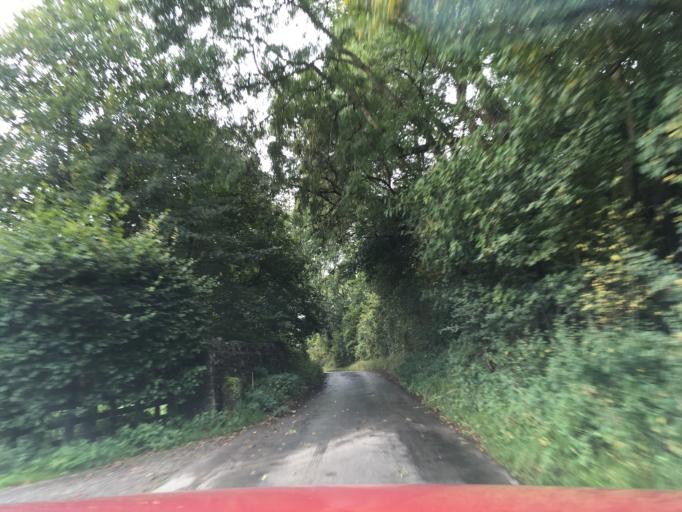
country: GB
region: England
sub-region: South Gloucestershire
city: Tytherington
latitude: 51.5957
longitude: -2.4720
